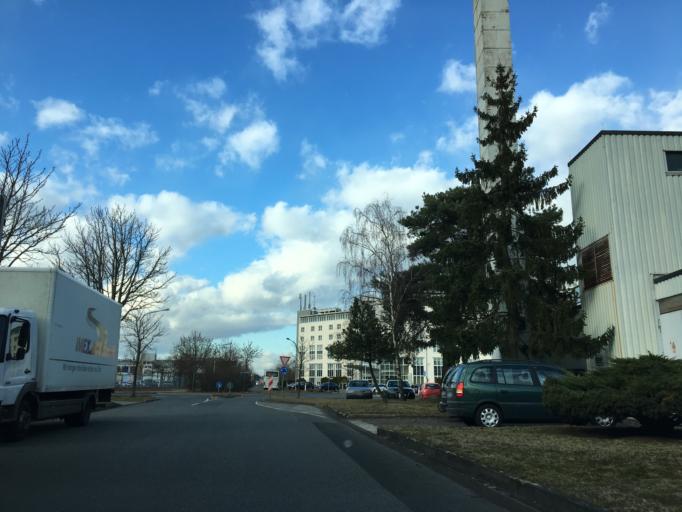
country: DE
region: Hesse
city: Morfelden-Walldorf
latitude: 49.9833
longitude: 8.5850
